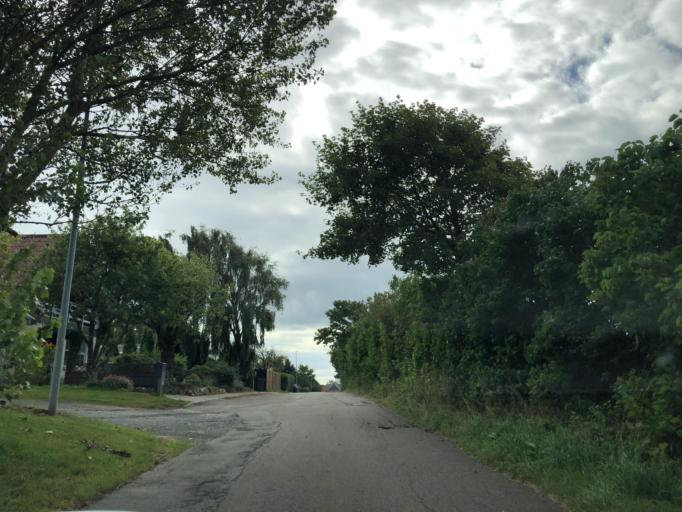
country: DK
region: North Denmark
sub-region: Vesthimmerland Kommune
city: Aars
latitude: 56.8150
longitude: 9.6532
